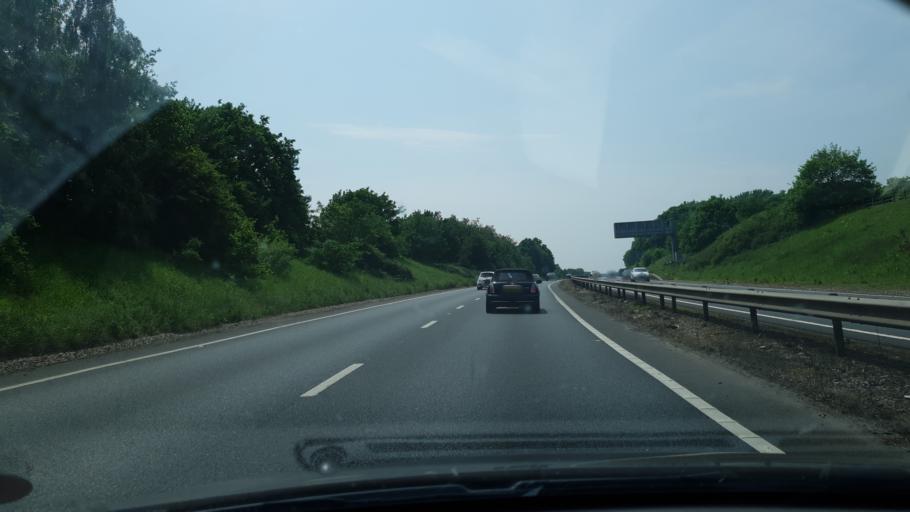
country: GB
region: England
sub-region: Suffolk
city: Bramford
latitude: 52.0269
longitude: 1.0921
